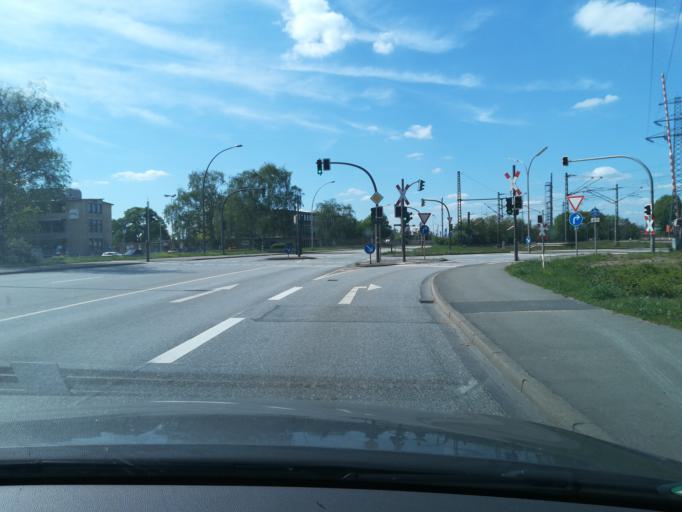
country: DE
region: Hamburg
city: Harburg
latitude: 53.4806
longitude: 9.9811
